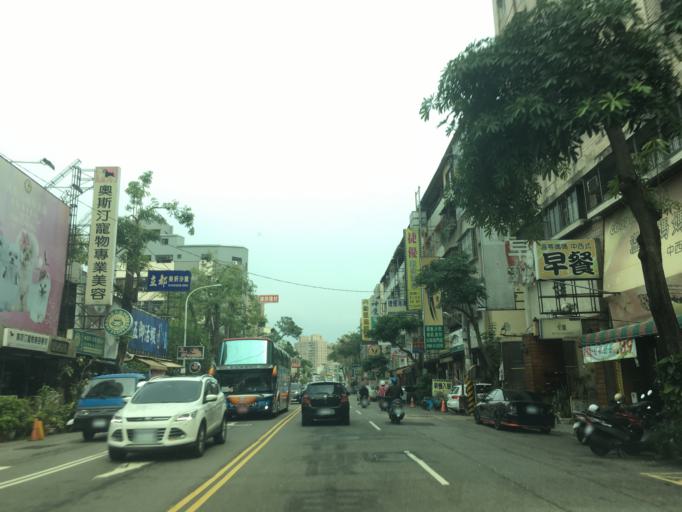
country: TW
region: Taiwan
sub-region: Taichung City
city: Taichung
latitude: 24.1670
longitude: 120.6852
